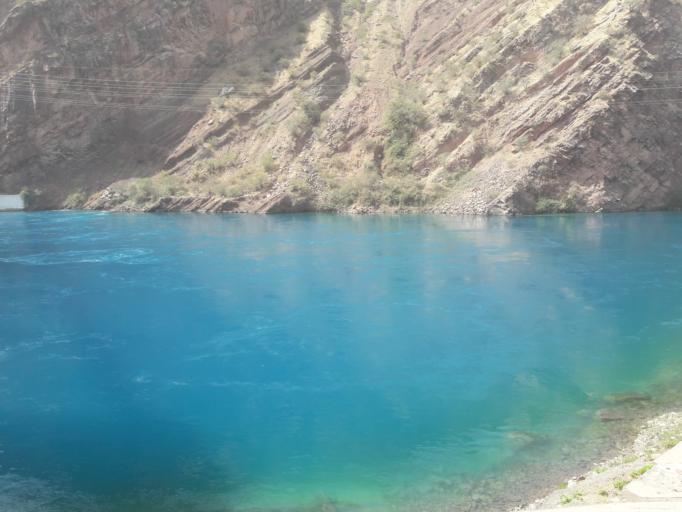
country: TJ
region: Khatlon
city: Norak
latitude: 38.3785
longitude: 69.3512
